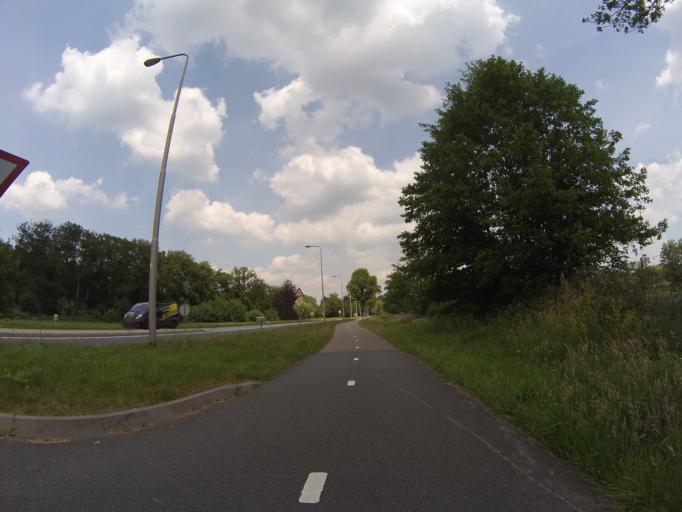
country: NL
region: Utrecht
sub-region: Gemeente Soest
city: Soest
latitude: 52.1685
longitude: 5.2420
